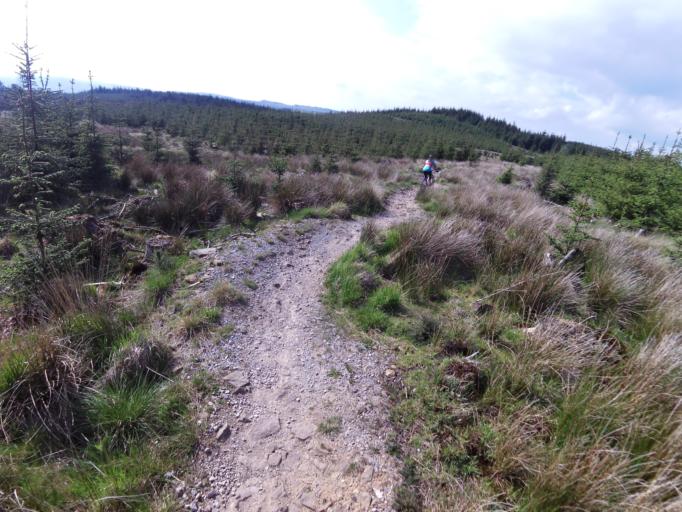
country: GB
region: England
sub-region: North Yorkshire
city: Settle
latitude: 54.0194
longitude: -2.3710
